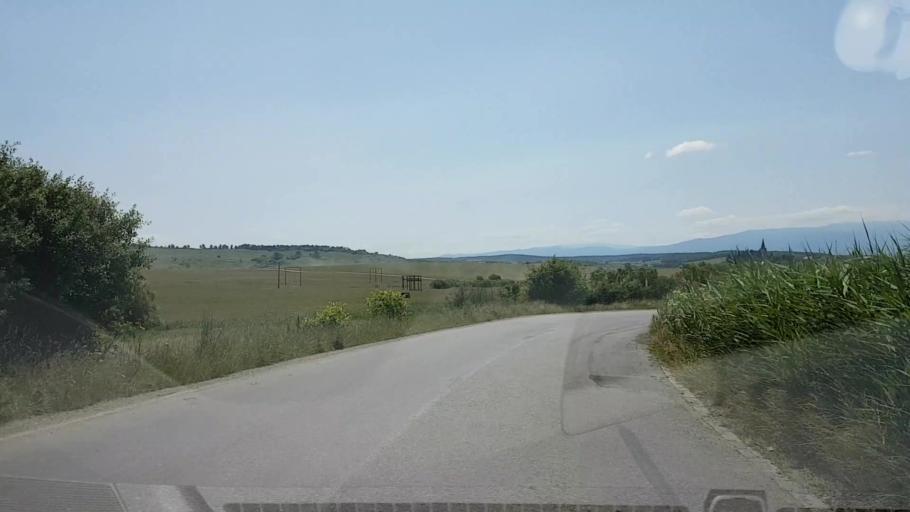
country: RO
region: Brasov
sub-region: Comuna Cincu
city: Cincu
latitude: 45.9324
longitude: 24.7951
